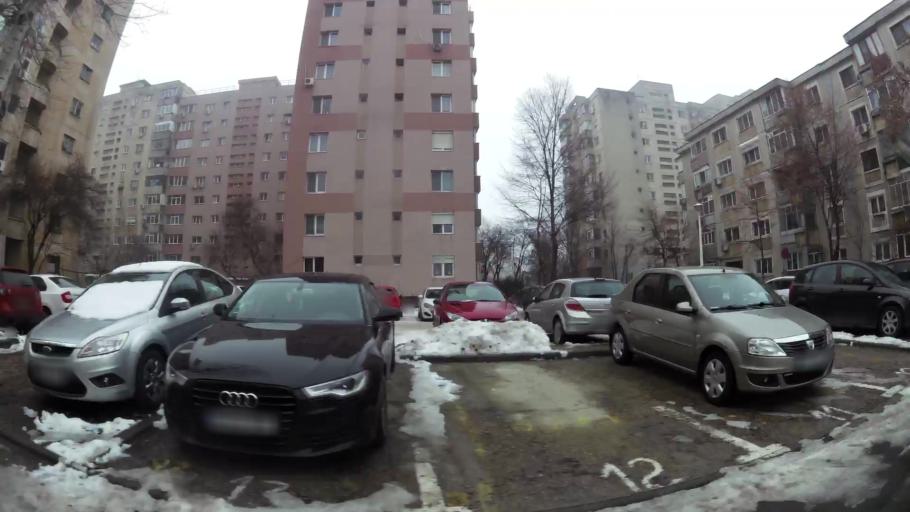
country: RO
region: Ilfov
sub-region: Comuna Chiajna
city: Rosu
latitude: 44.4534
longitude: 26.0422
